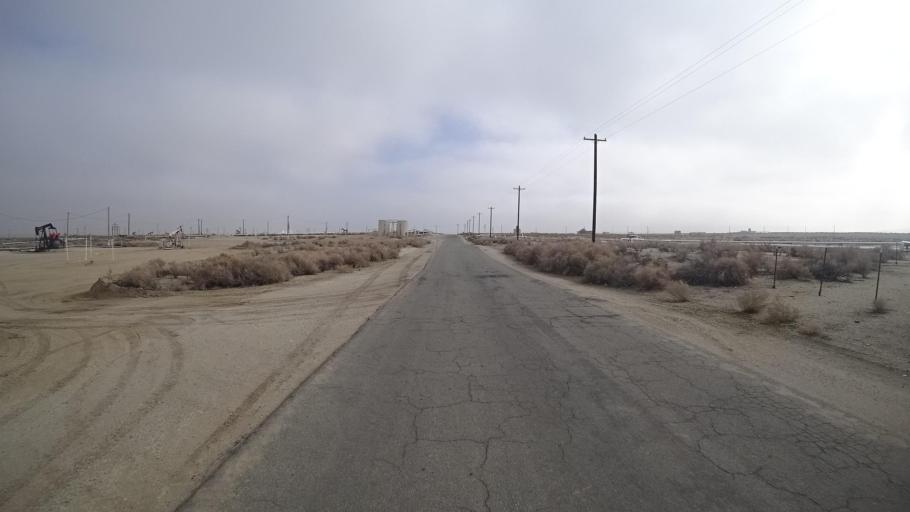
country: US
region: California
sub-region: Kern County
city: Maricopa
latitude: 35.0342
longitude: -119.3519
